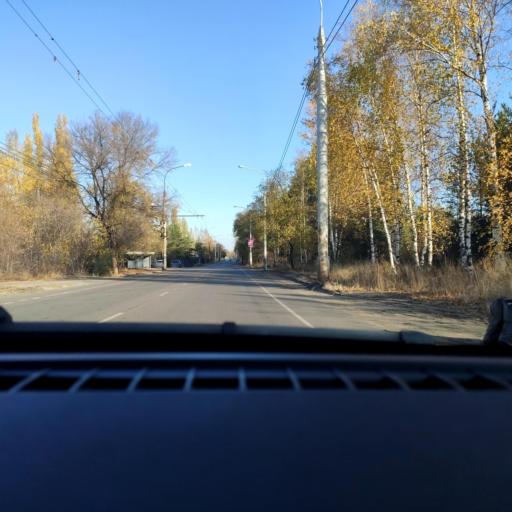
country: RU
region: Voronezj
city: Somovo
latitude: 51.7122
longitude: 39.2928
